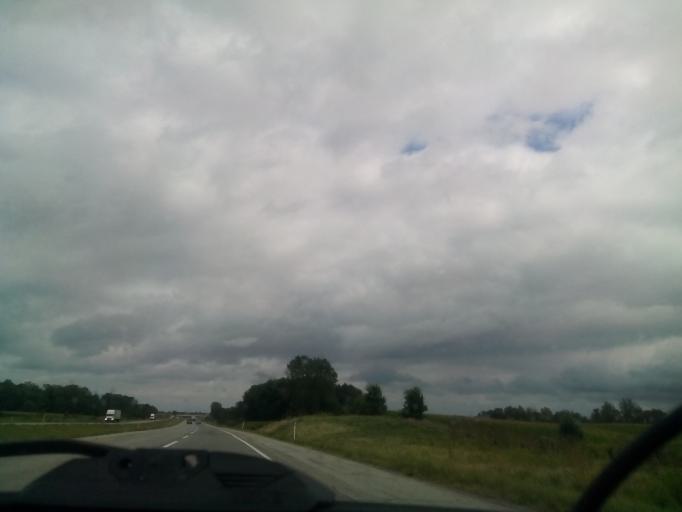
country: US
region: Indiana
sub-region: Steuben County
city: Fremont
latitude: 41.6931
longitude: -84.9050
